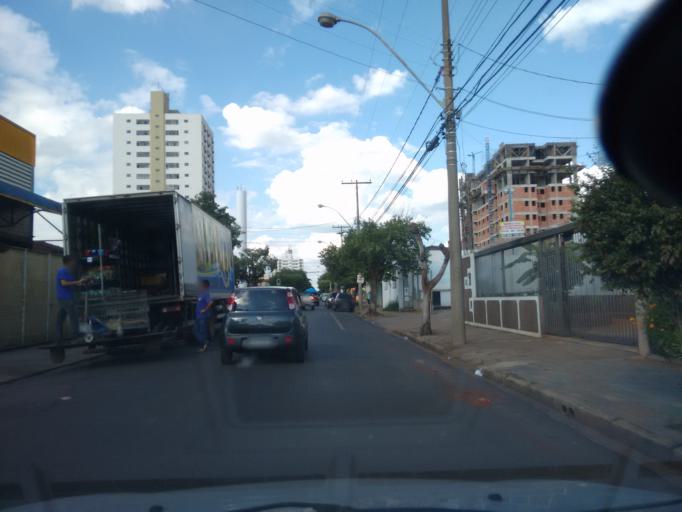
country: BR
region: Sao Paulo
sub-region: Araraquara
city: Araraquara
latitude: -21.7993
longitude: -48.1844
